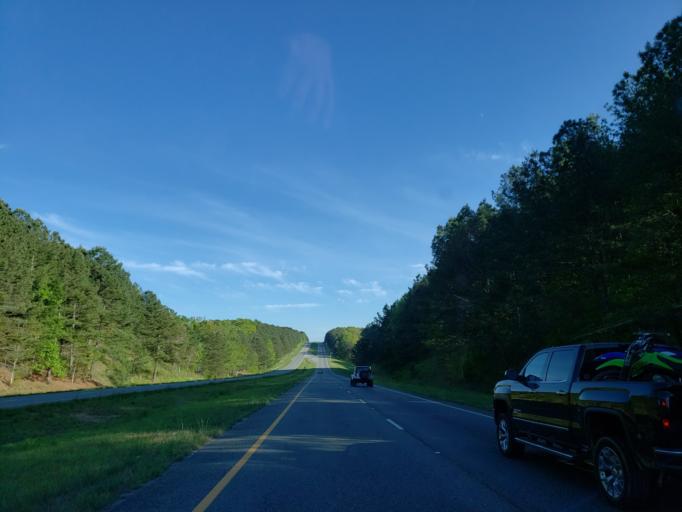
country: US
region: Georgia
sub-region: Polk County
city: Rockmart
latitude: 33.9567
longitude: -84.9851
